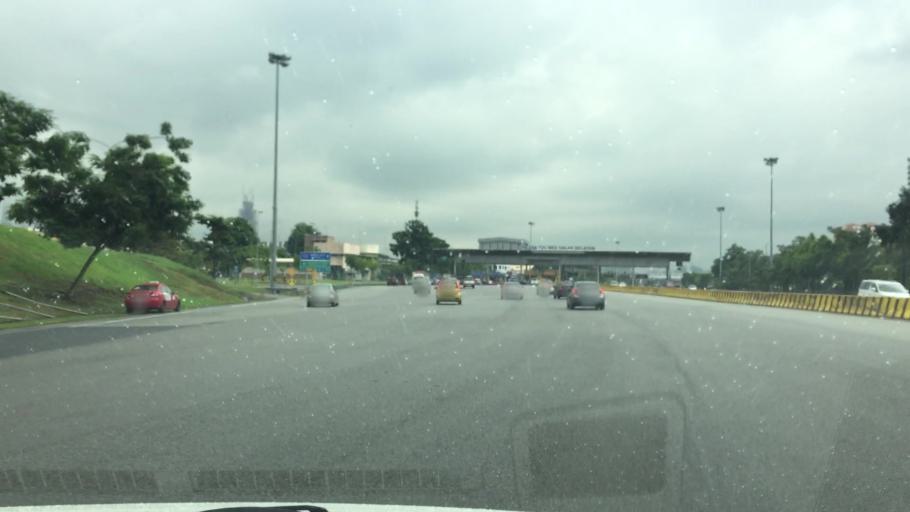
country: MY
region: Kuala Lumpur
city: Kuala Lumpur
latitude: 3.1085
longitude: 101.7105
